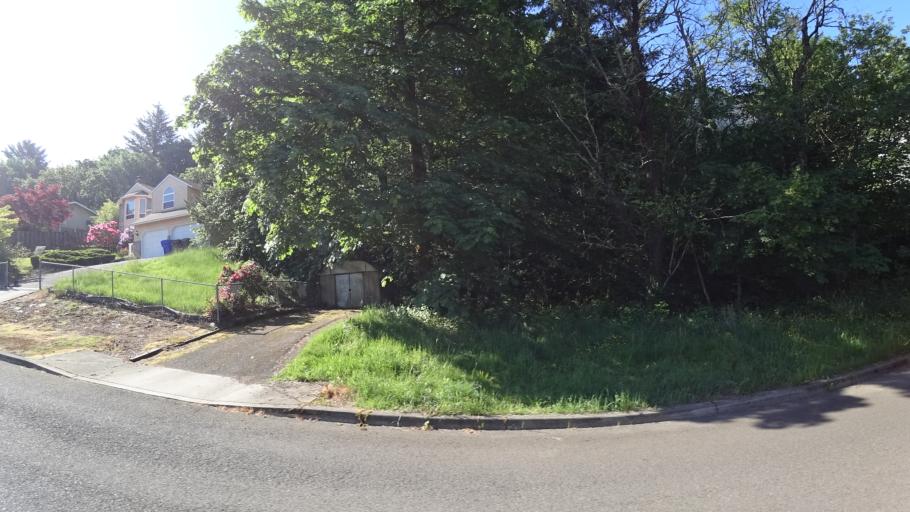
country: US
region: Oregon
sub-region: Clackamas County
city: Happy Valley
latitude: 45.4661
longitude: -122.5414
